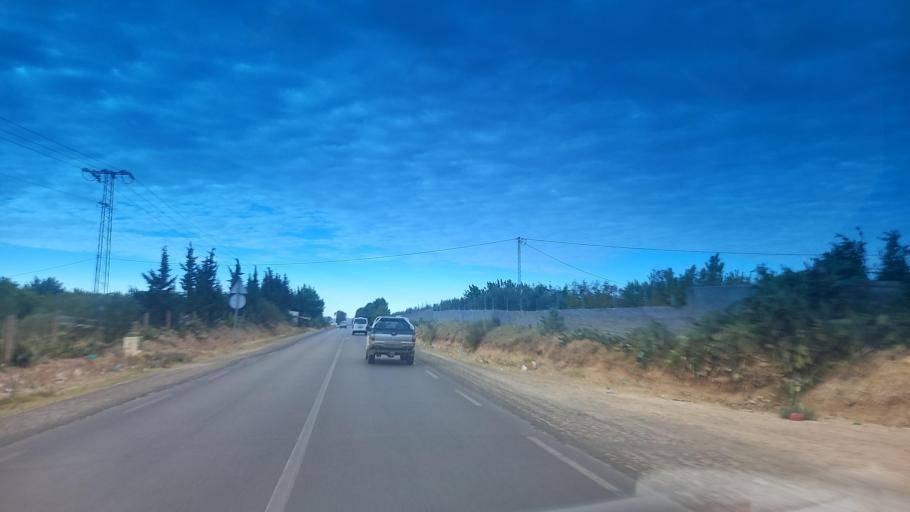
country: TN
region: Al Qasrayn
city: Sbiba
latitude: 35.2774
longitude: 9.0937
